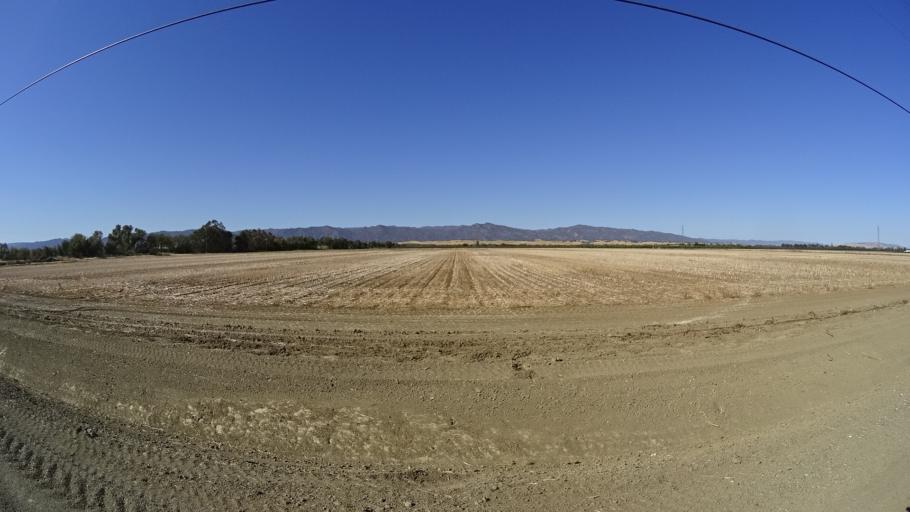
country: US
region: California
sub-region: Yolo County
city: Cottonwood
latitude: 38.6077
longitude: -121.9714
